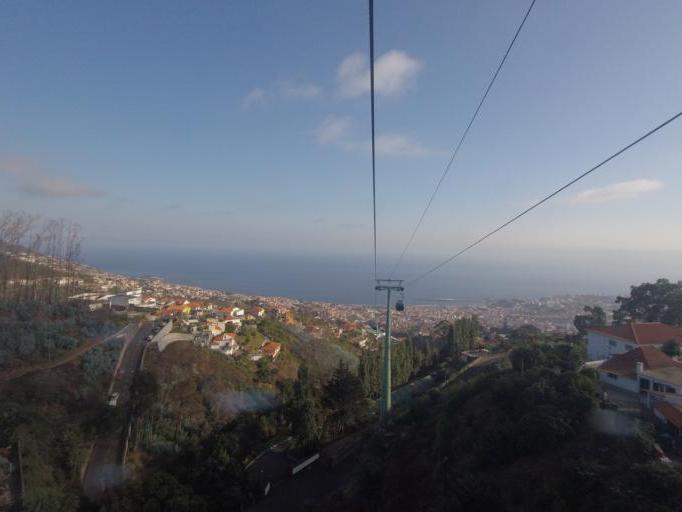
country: PT
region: Madeira
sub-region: Funchal
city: Nossa Senhora do Monte
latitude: 32.6745
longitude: -16.9003
